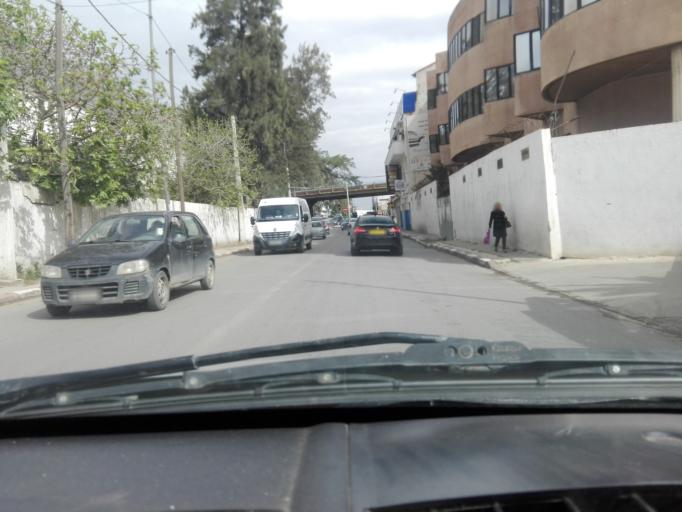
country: DZ
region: Alger
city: Bab Ezzouar
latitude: 36.7294
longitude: 3.1309
